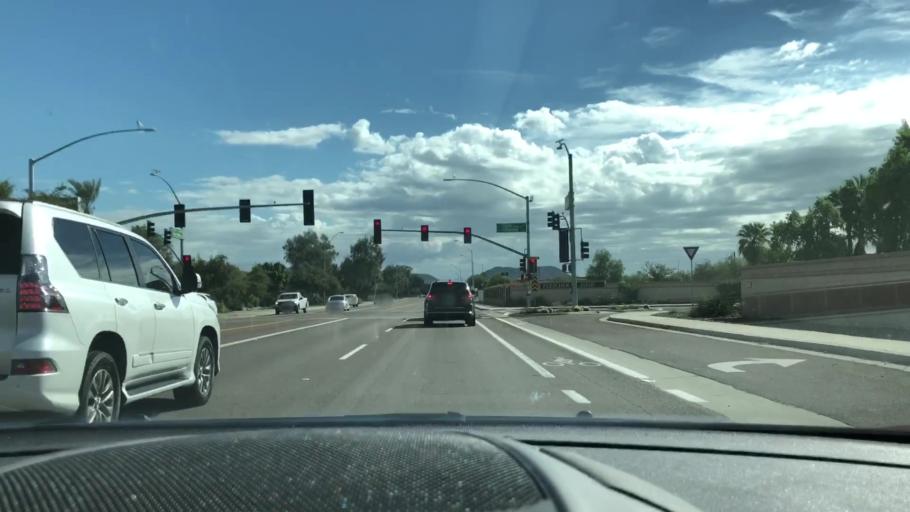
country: US
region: Arizona
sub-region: Maricopa County
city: Sun City
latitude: 33.6816
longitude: -112.2296
